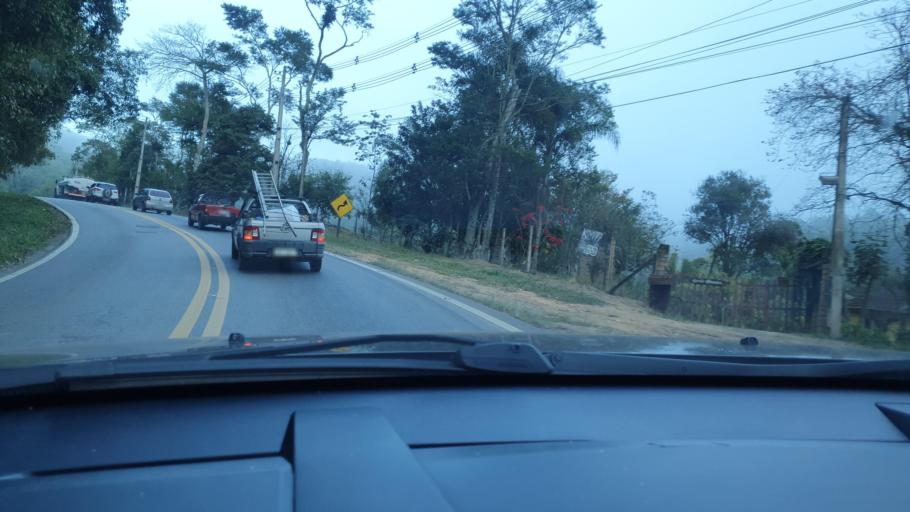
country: BR
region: Sao Paulo
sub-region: Ibiuna
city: Ibiuna
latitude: -23.6840
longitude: -47.2656
